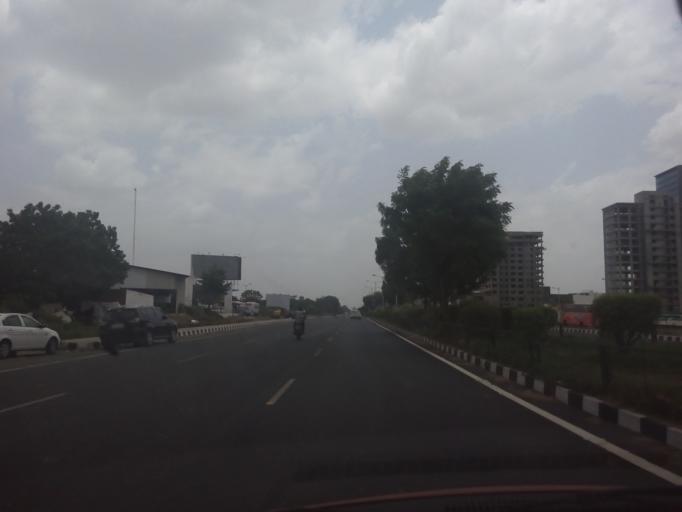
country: IN
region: Gujarat
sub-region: Ahmadabad
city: Sarkhej
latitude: 23.0012
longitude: 72.4992
